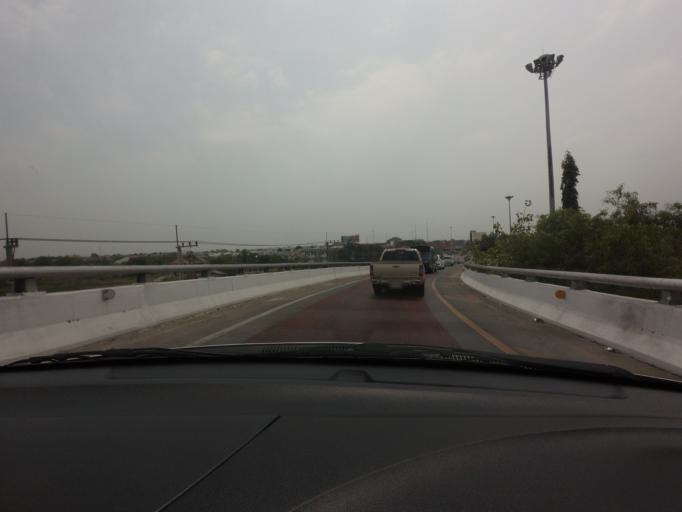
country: TH
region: Bangkok
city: Thawi Watthana
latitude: 13.7894
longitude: 100.3286
